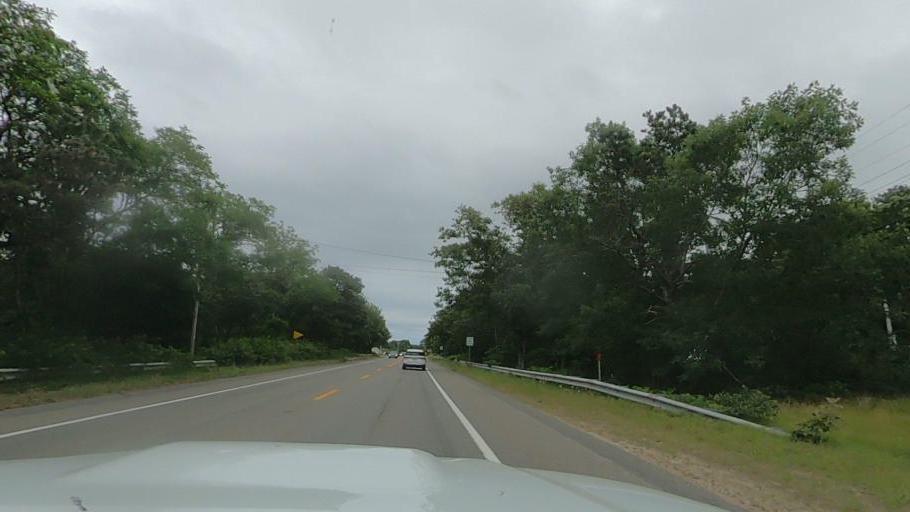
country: US
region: Massachusetts
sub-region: Barnstable County
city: Wellfleet
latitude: 41.9175
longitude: -69.9968
